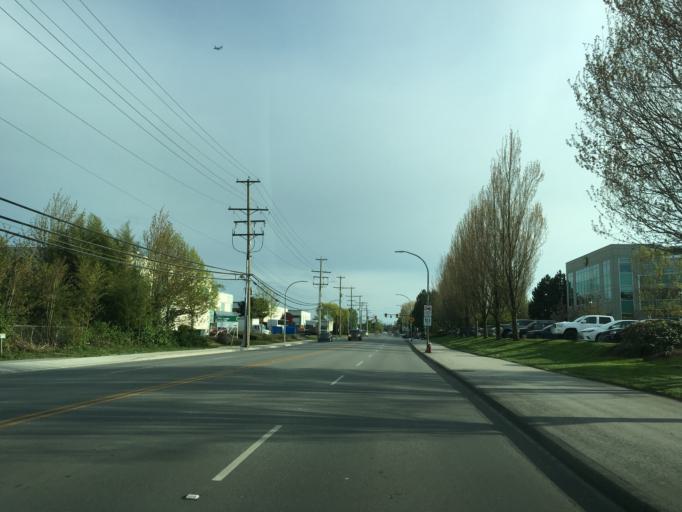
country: CA
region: British Columbia
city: Richmond
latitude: 49.1732
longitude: -123.0693
